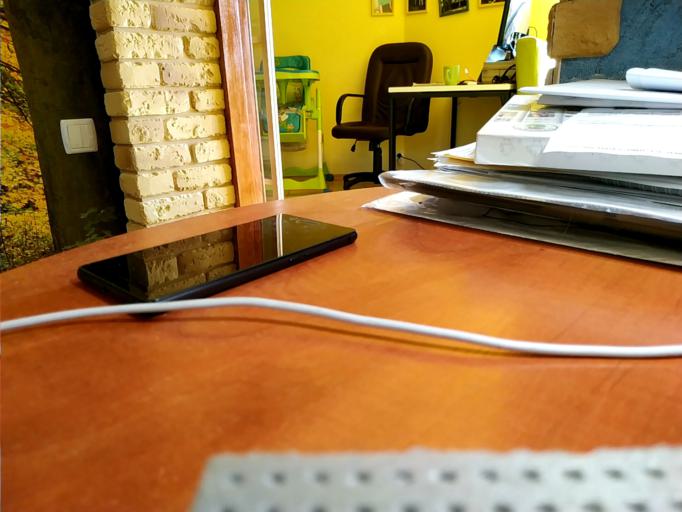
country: RU
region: Tverskaya
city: Kalashnikovo
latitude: 57.3715
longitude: 35.4082
